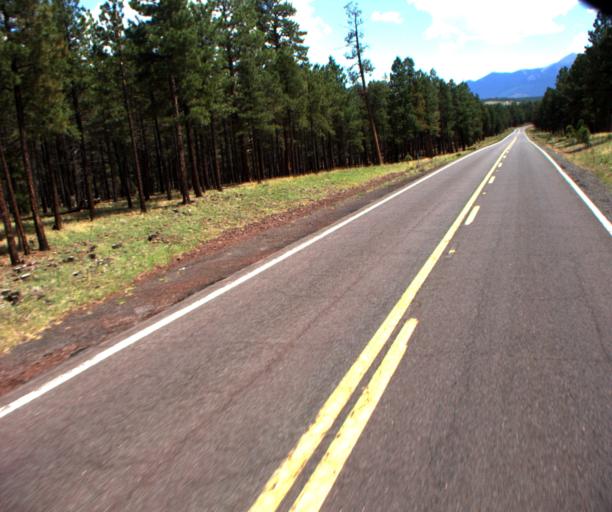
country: US
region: Arizona
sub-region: Coconino County
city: Parks
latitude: 35.4636
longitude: -111.7822
